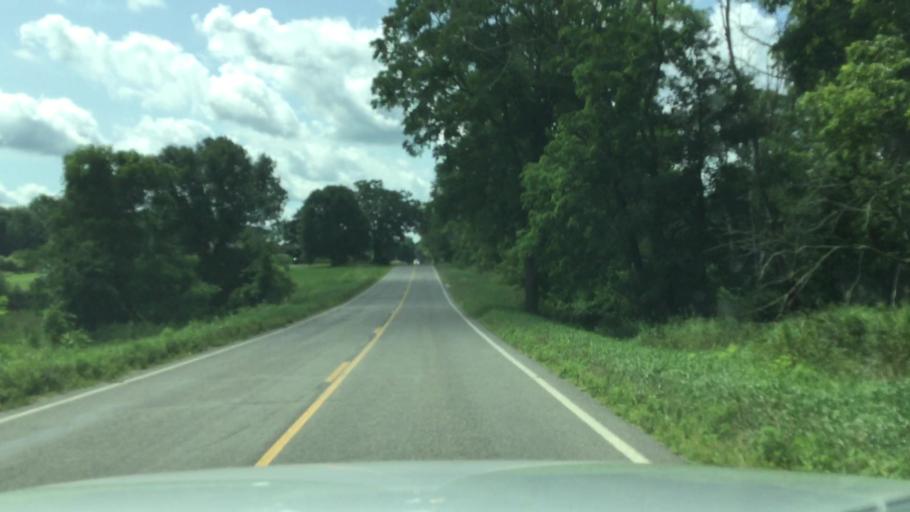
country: US
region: Michigan
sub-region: Montcalm County
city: Greenville
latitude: 43.1542
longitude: -85.2136
